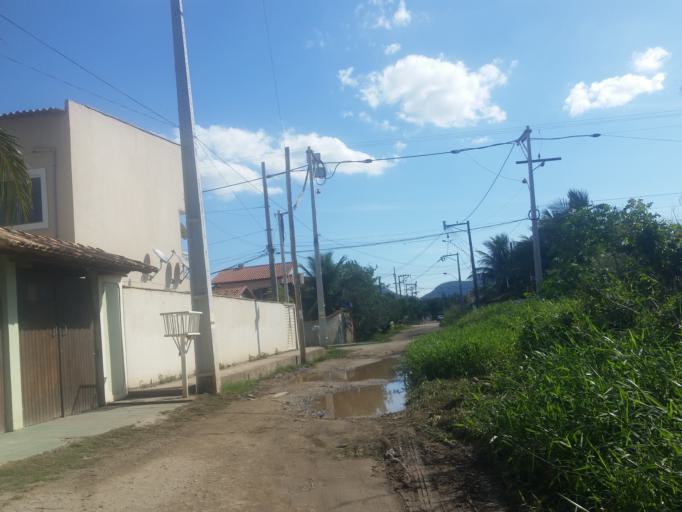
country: BR
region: Rio de Janeiro
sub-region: Marica
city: Marica
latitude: -22.9621
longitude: -42.9645
